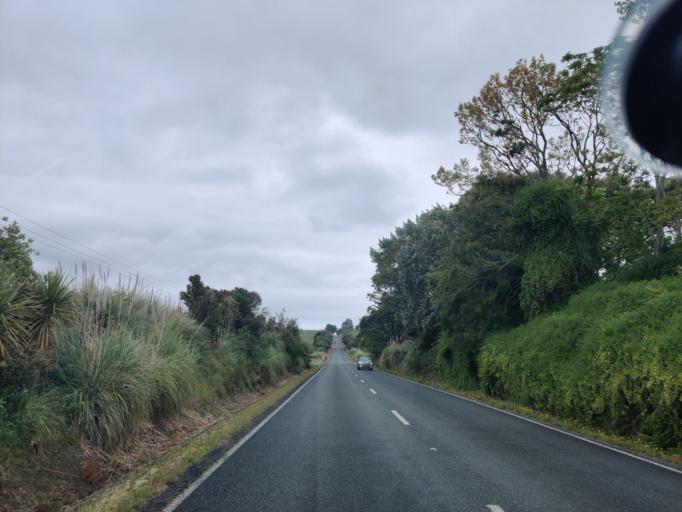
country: NZ
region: Northland
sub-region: Kaipara District
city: Dargaville
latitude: -36.1282
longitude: 174.1255
